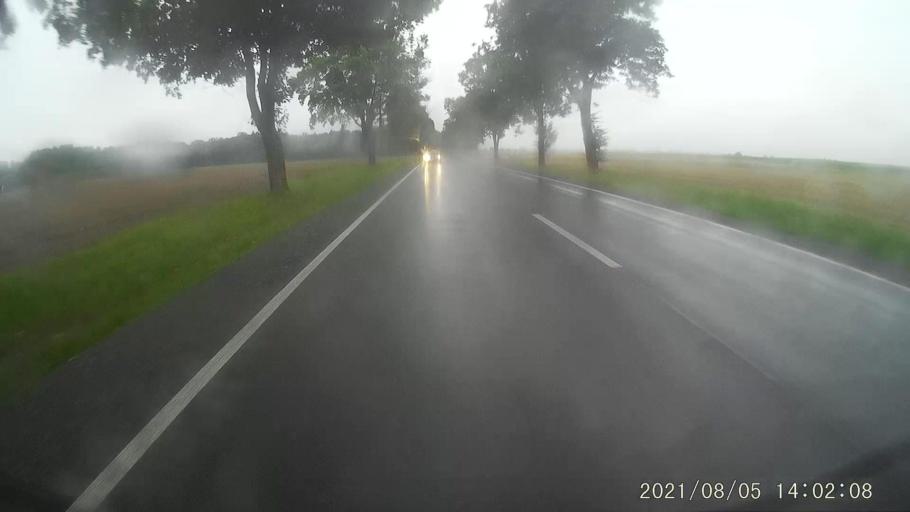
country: PL
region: Opole Voivodeship
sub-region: Powiat krapkowicki
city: Strzeleczki
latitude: 50.4533
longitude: 17.8804
